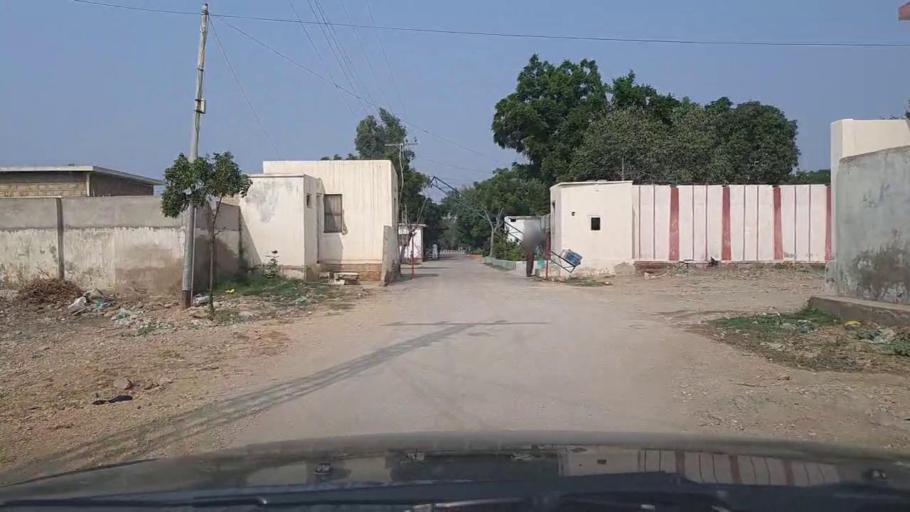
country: PK
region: Sindh
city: Thatta
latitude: 24.7447
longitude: 67.8944
